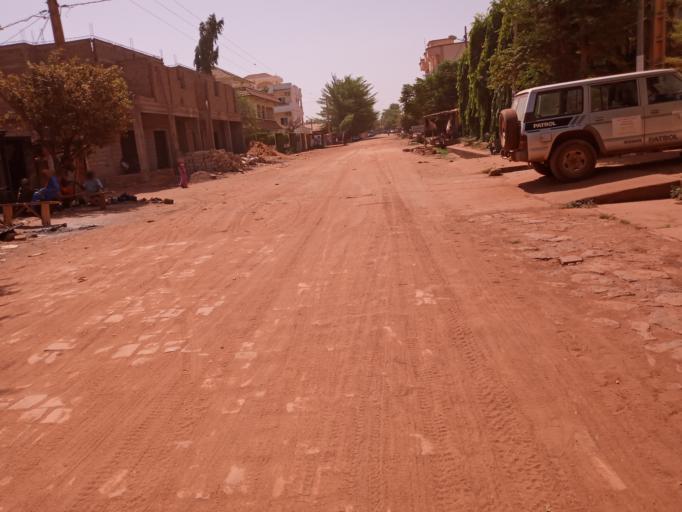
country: ML
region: Bamako
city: Bamako
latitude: 12.5858
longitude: -7.9555
